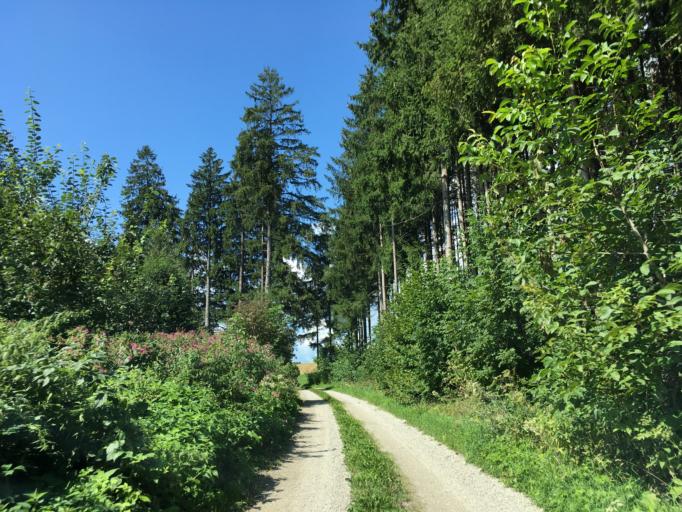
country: DE
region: Bavaria
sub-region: Upper Bavaria
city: Amerang
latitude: 47.9859
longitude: 12.3405
